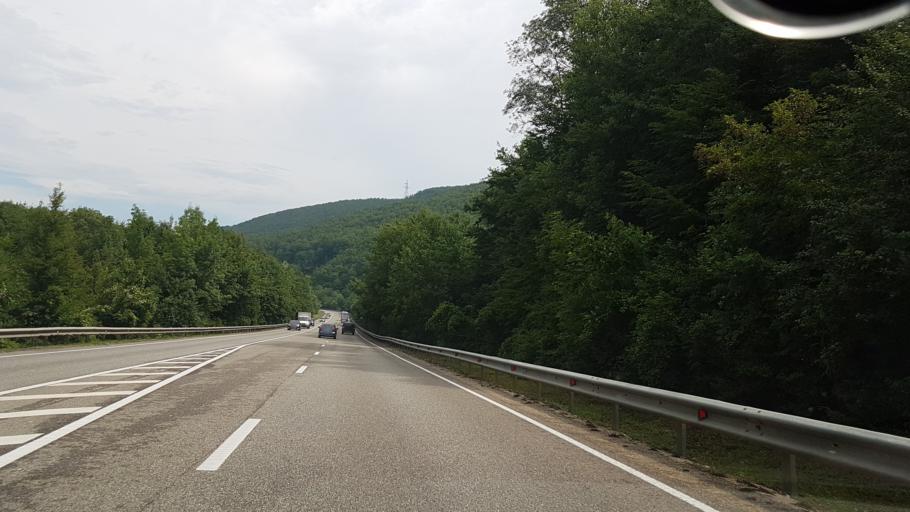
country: RU
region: Krasnodarskiy
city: Goryachiy Klyuch
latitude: 44.5634
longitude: 39.0004
